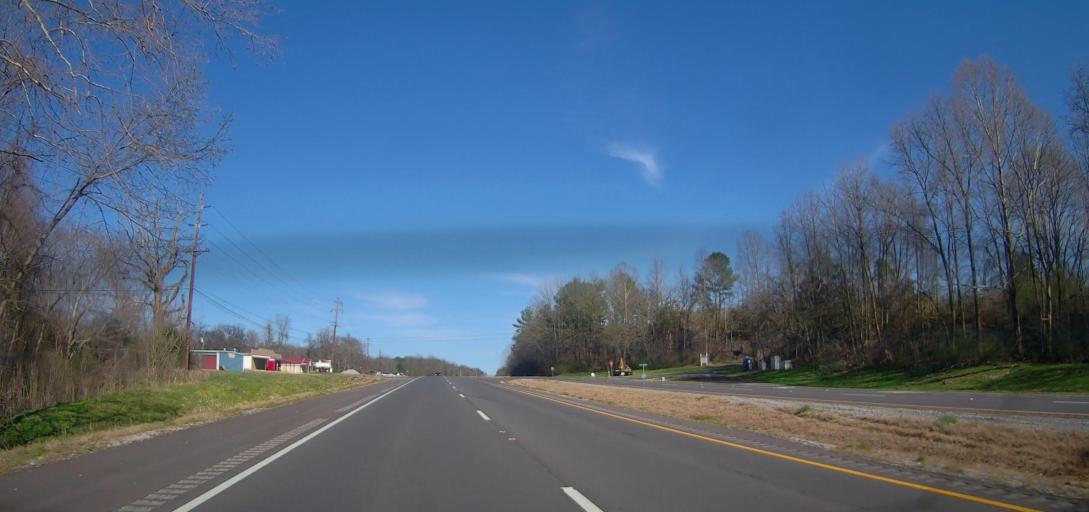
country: US
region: Alabama
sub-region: Lauderdale County
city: Killen
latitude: 34.8597
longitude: -87.5253
